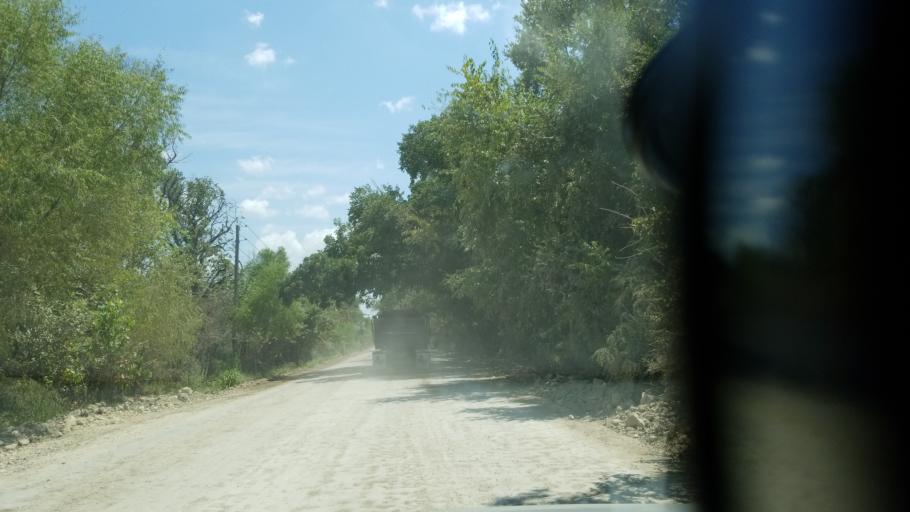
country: US
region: Texas
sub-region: Dallas County
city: Farmers Branch
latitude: 32.8790
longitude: -96.9198
